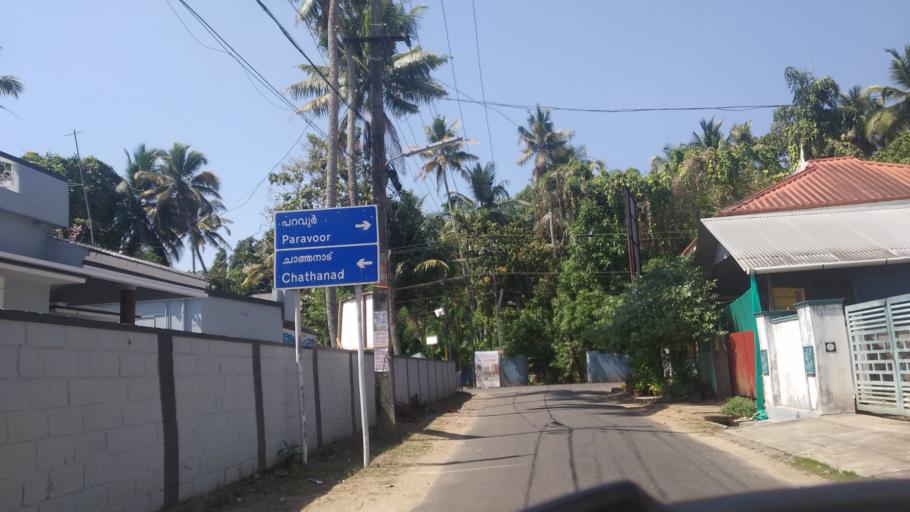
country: IN
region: Kerala
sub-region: Ernakulam
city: Elur
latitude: 10.1349
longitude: 76.2260
